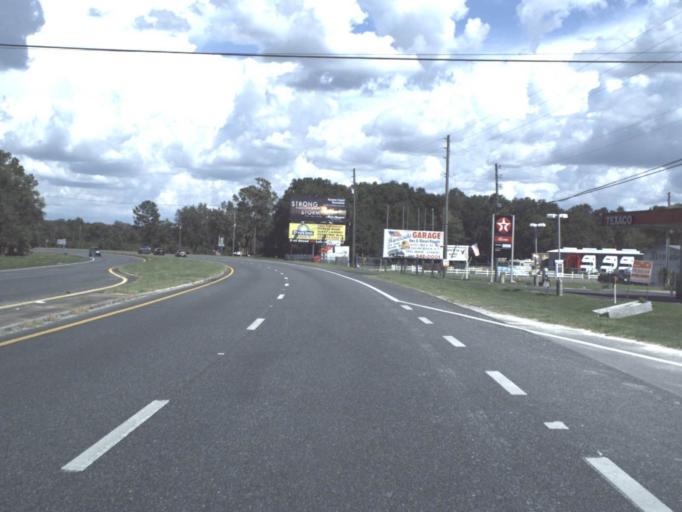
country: US
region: Florida
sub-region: Levy County
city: Manatee Road
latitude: 29.5848
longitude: -82.9569
